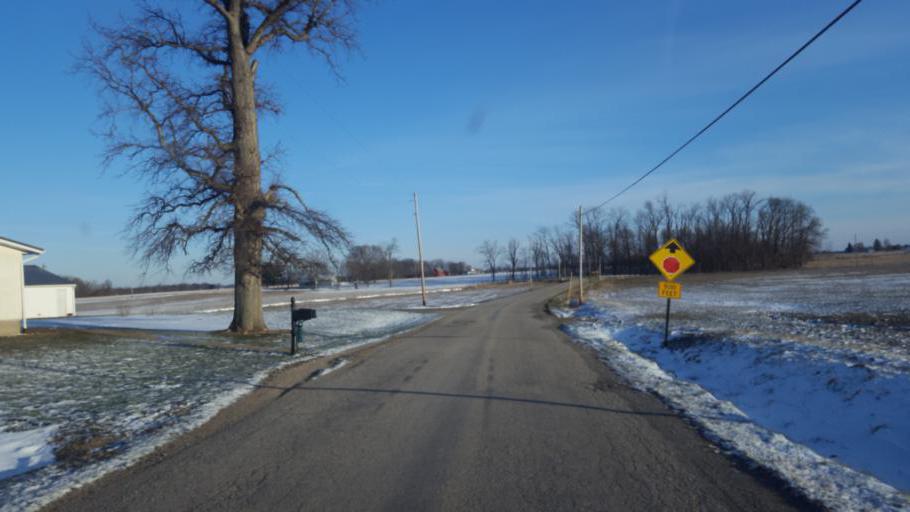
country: US
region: Ohio
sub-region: Morrow County
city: Cardington
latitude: 40.5262
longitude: -82.9050
